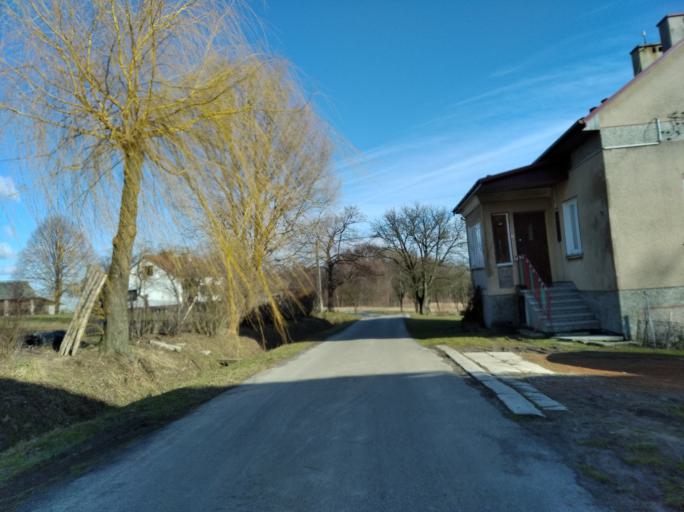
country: PL
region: Subcarpathian Voivodeship
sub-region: Powiat strzyzowski
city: Wisniowa
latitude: 49.8994
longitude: 21.6699
